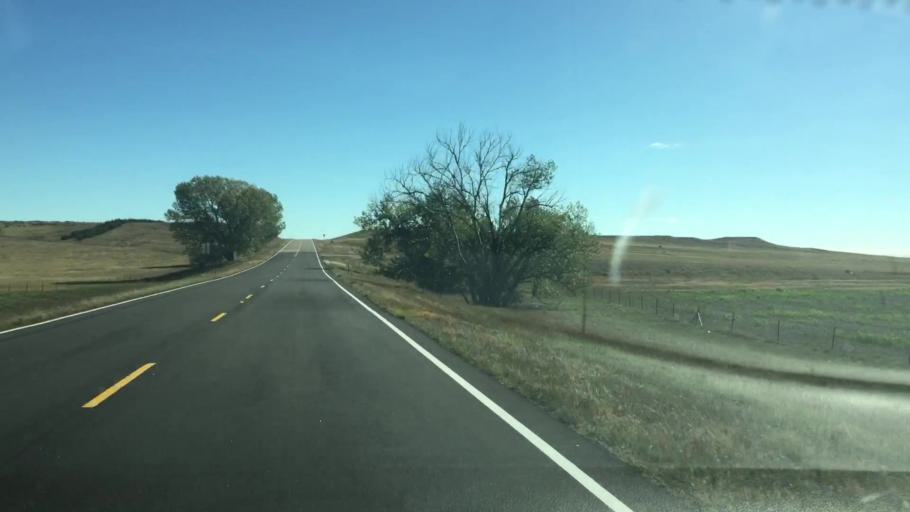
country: US
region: Colorado
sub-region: Lincoln County
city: Limon
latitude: 39.2950
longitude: -103.8847
